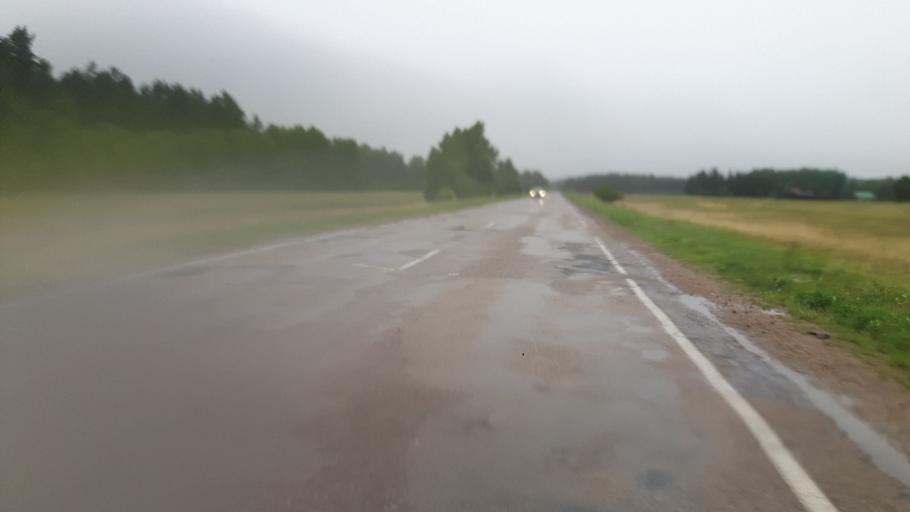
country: LV
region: Rucavas
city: Rucava
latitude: 56.0986
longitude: 21.1321
